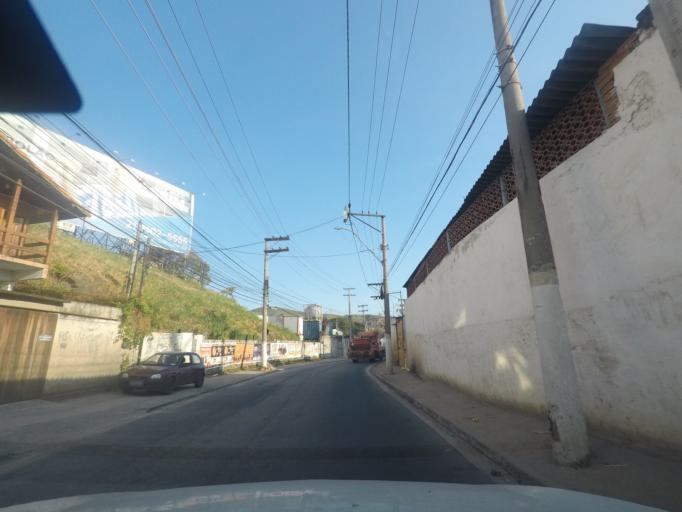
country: BR
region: Rio de Janeiro
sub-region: Niteroi
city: Niteroi
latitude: -22.8763
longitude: -43.1147
